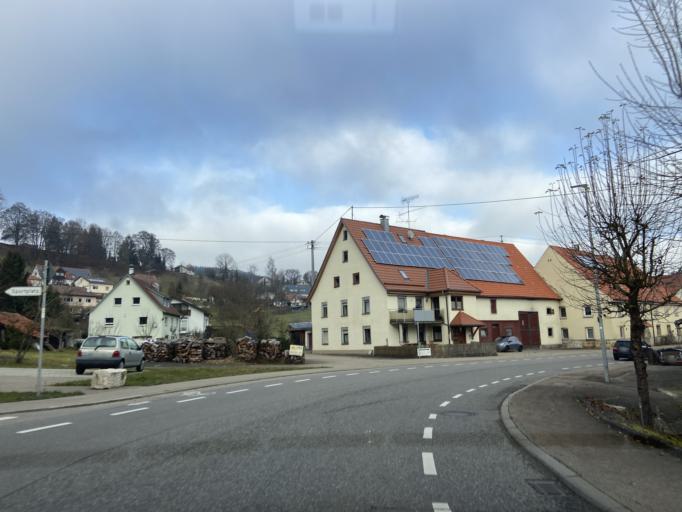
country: DE
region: Baden-Wuerttemberg
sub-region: Tuebingen Region
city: Gammertingen
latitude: 48.2612
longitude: 9.2055
